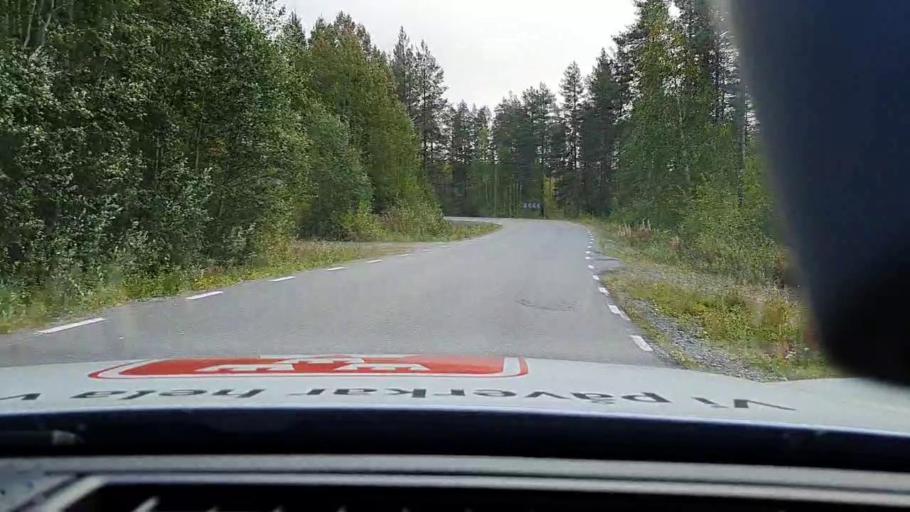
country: SE
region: Vaesterbotten
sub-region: Skelleftea Kommun
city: Langsele
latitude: 64.9398
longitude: 20.0033
